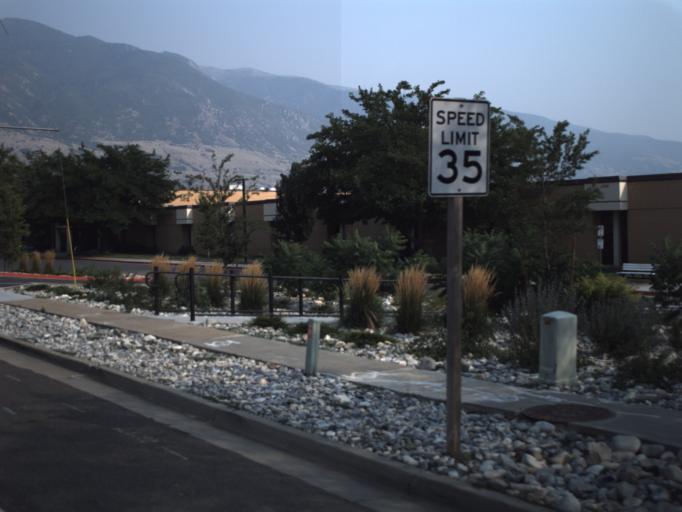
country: US
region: Utah
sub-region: Davis County
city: Farmington
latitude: 41.0007
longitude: -111.9060
